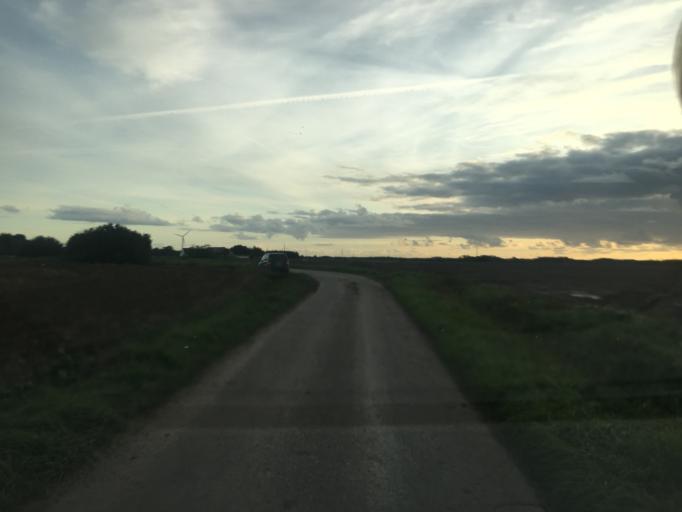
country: DK
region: South Denmark
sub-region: Tonder Kommune
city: Tonder
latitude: 54.9751
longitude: 8.9050
